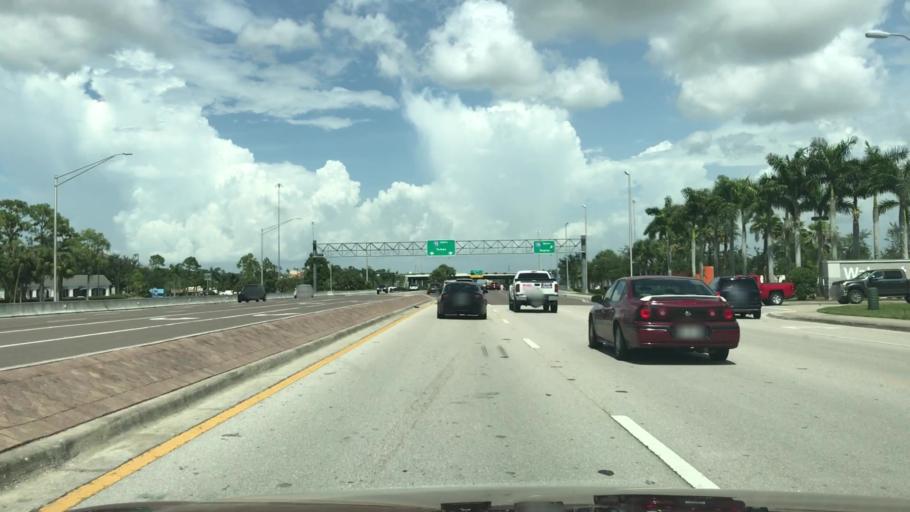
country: US
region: Florida
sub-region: Collier County
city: Vineyards
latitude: 26.2728
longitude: -81.7468
